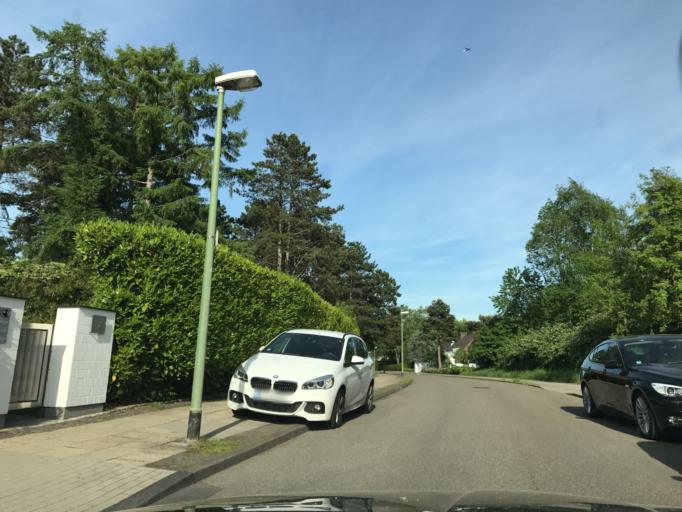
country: DE
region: North Rhine-Westphalia
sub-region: Regierungsbezirk Dusseldorf
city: Essen
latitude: 51.4073
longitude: 6.9782
